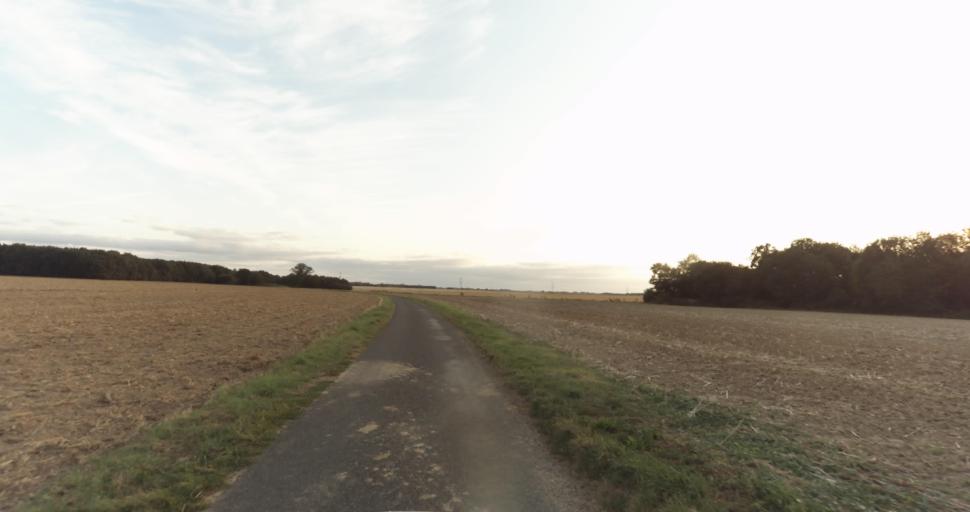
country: FR
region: Haute-Normandie
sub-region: Departement de l'Eure
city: La Madeleine-de-Nonancourt
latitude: 48.8637
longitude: 1.2241
